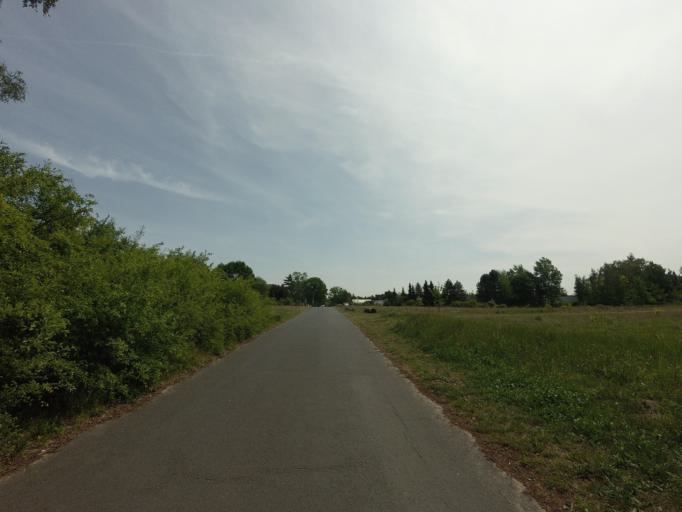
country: DE
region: Lower Saxony
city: Klein Schwulper
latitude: 52.3103
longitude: 10.4789
